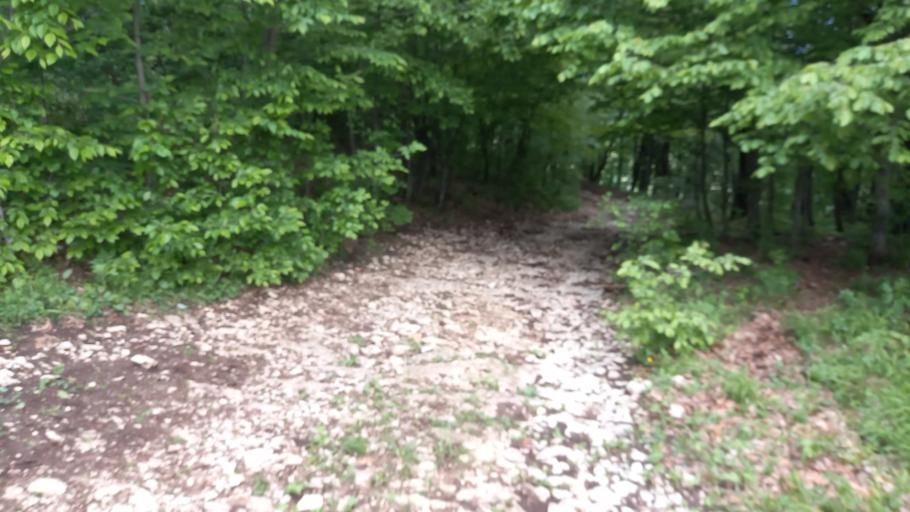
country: RU
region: Adygeya
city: Kamennomostskiy
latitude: 44.2225
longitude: 40.0018
